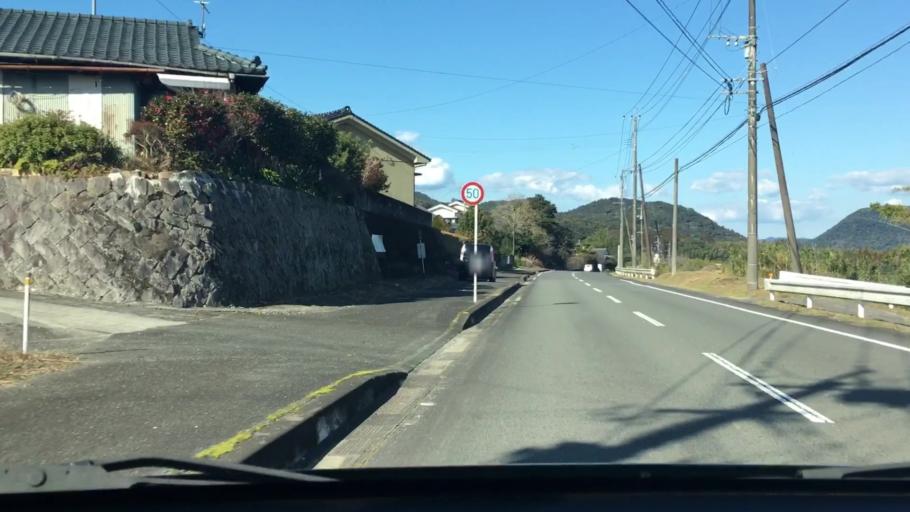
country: JP
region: Kagoshima
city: Satsumasendai
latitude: 31.7714
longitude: 130.4014
